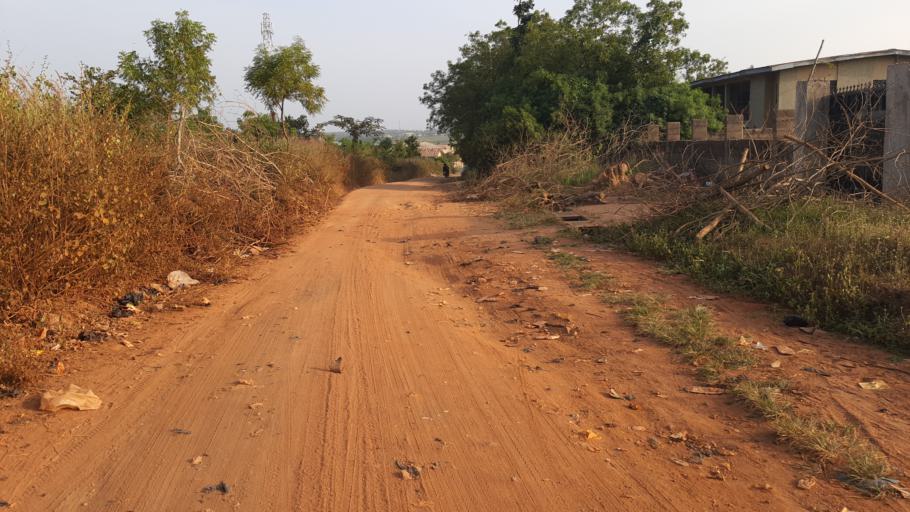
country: NG
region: Osun
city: Iwo
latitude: 7.6256
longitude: 4.1575
